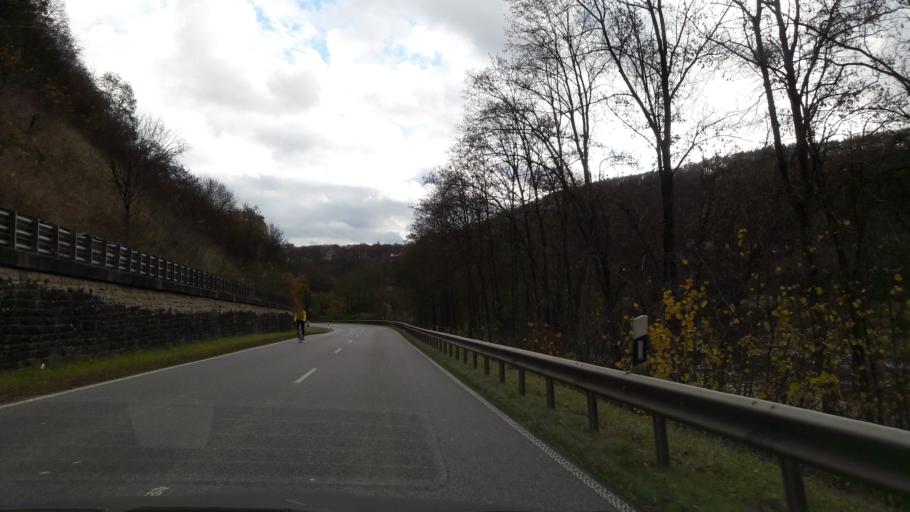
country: DE
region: Rheinland-Pfalz
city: Menningen
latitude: 49.8176
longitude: 6.4826
